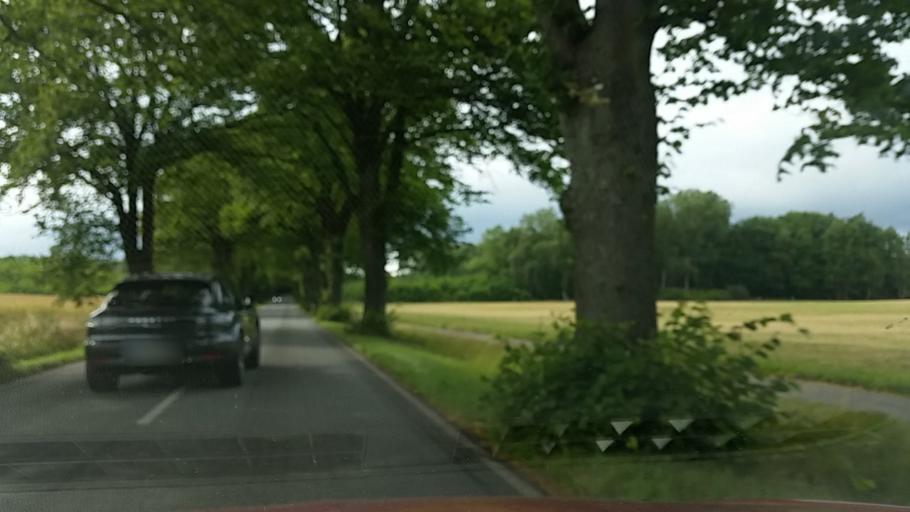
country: DE
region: Mecklenburg-Vorpommern
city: Ostseebad Kuhlungsborn
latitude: 54.1352
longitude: 11.7848
